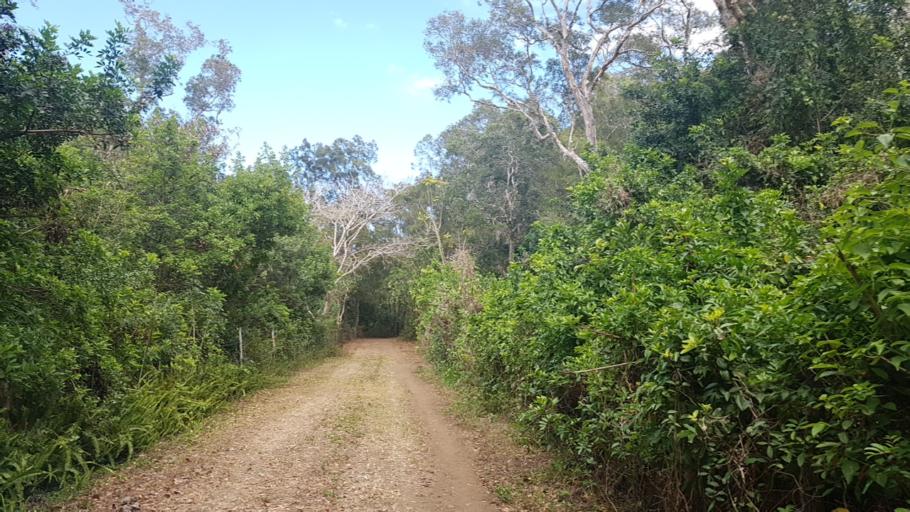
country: NC
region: South Province
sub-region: Dumbea
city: Dumbea
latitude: -22.1775
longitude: 166.4786
